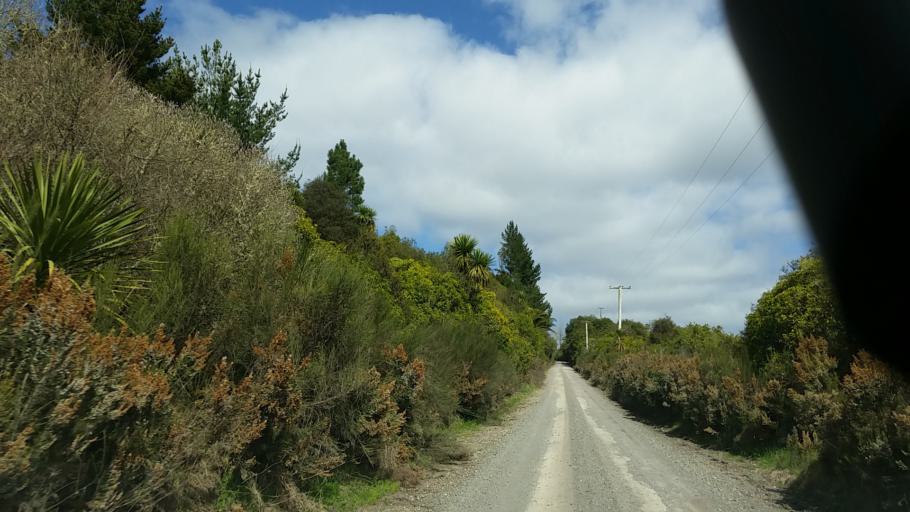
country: NZ
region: Bay of Plenty
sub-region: Rotorua District
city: Rotorua
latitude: -38.4023
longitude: 176.1430
